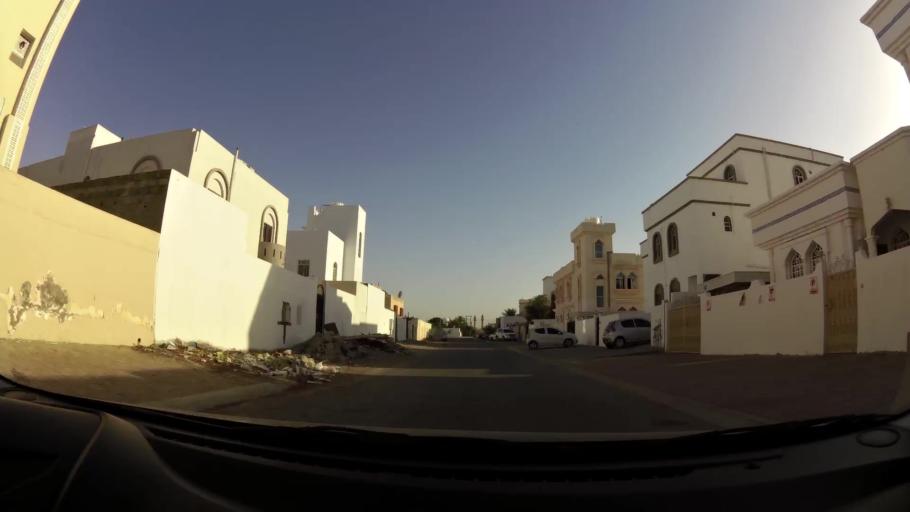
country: OM
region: Muhafazat Masqat
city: As Sib al Jadidah
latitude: 23.6329
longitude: 58.1938
